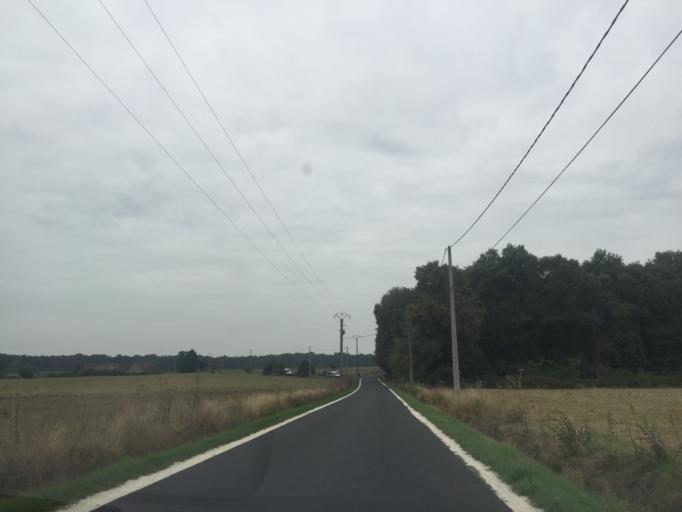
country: FR
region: Centre
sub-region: Departement d'Indre-et-Loire
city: Auzouer-en-Touraine
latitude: 47.5174
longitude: 0.9904
